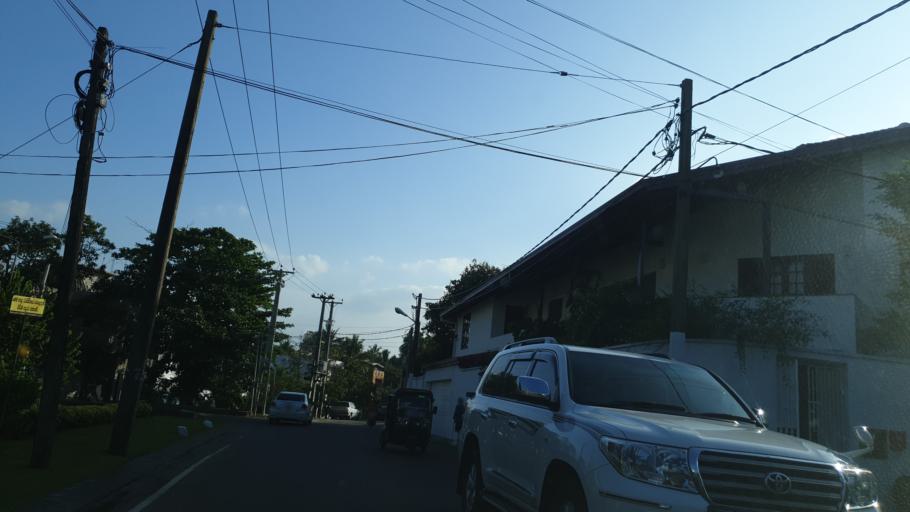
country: LK
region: Western
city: Galkissa
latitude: 6.8461
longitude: 79.8772
